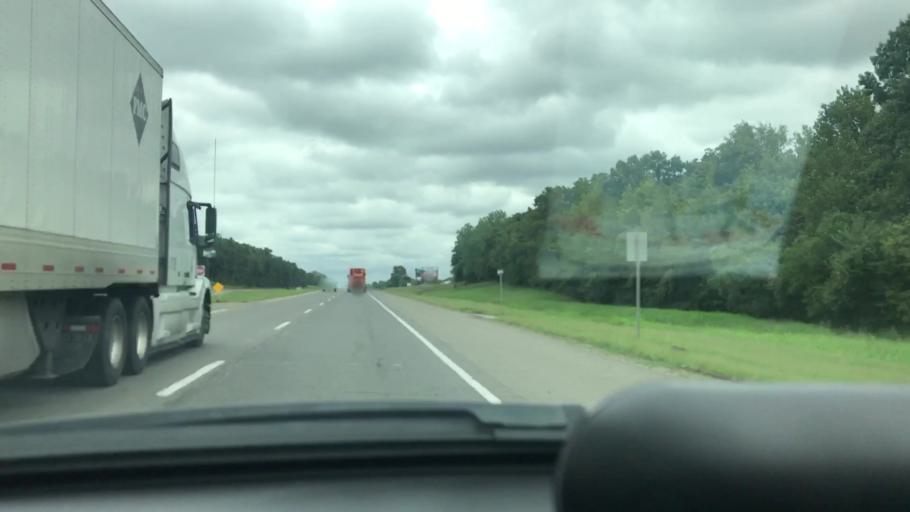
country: US
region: Oklahoma
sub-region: Muskogee County
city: Muskogee
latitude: 35.8214
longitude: -95.4026
